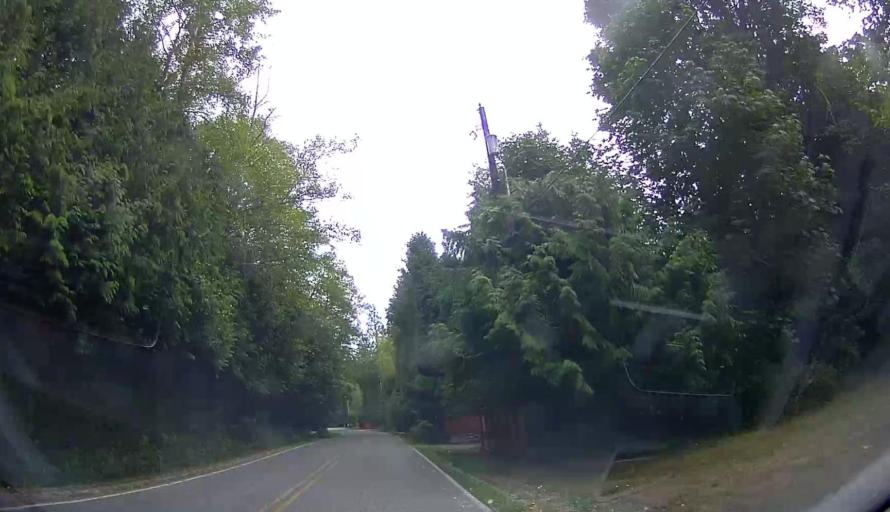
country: US
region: Washington
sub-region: Skagit County
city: Burlington
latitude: 48.5871
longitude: -122.3958
